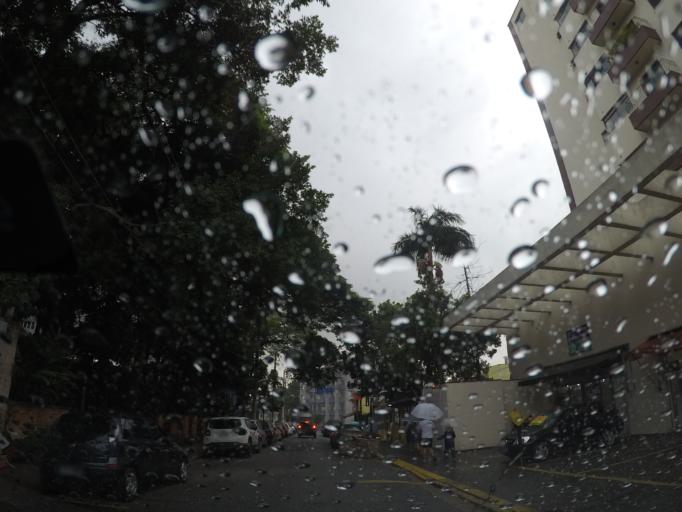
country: BR
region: Sao Paulo
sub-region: Diadema
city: Diadema
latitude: -23.6443
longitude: -46.6423
